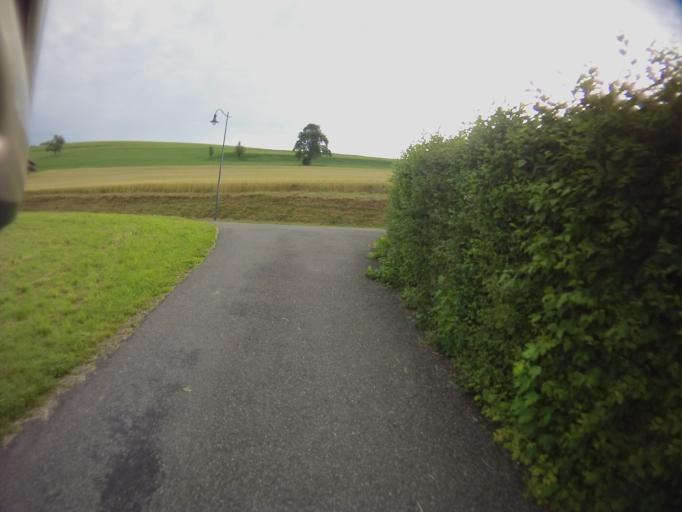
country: CH
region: Zurich
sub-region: Bezirk Affoltern
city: Knonau
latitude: 47.2168
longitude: 8.4728
